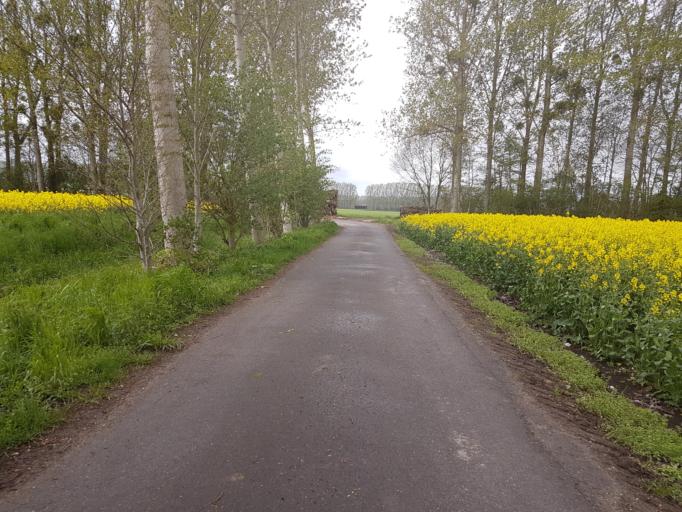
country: CH
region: Vaud
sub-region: Jura-Nord vaudois District
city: Montagny
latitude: 46.7572
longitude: 6.6114
